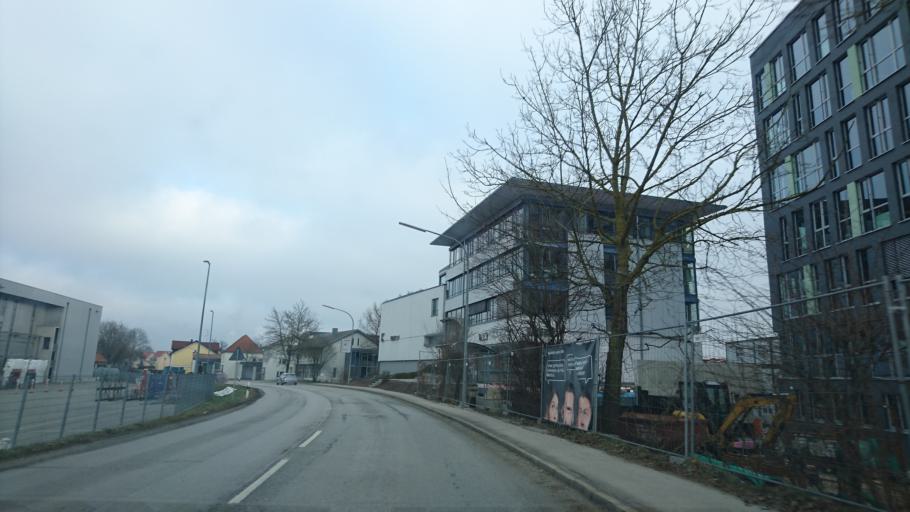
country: DE
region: Bavaria
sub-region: Lower Bavaria
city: Arnstorf
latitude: 48.5630
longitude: 12.8099
